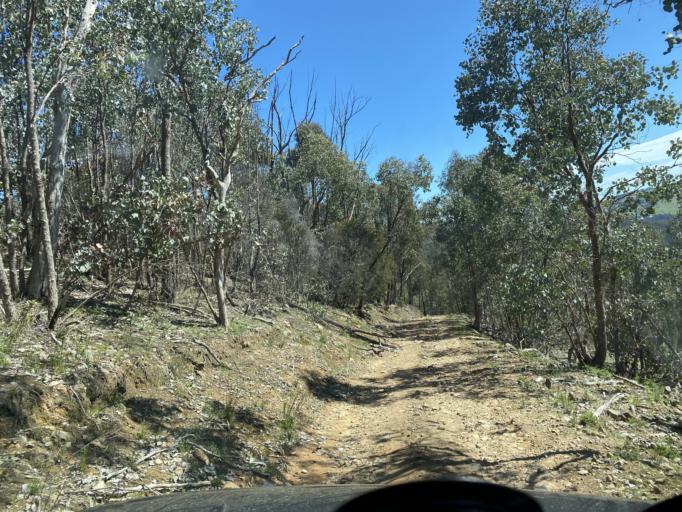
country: AU
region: Victoria
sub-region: Benalla
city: Benalla
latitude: -36.7200
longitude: 146.1821
